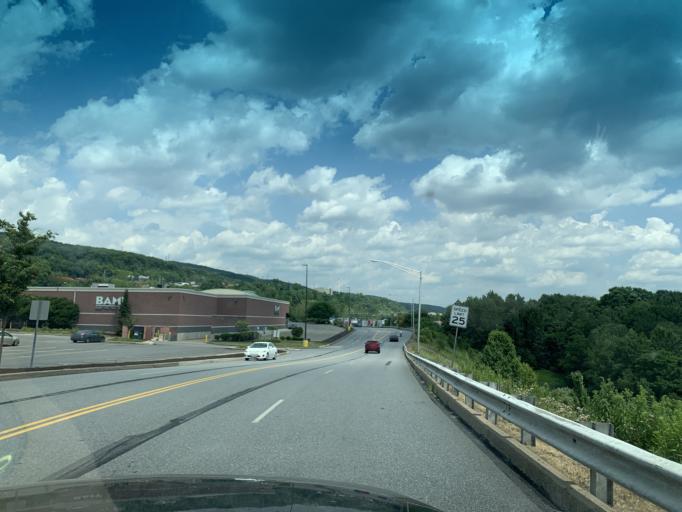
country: US
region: Pennsylvania
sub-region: Lackawanna County
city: Chinchilla
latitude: 41.4593
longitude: -75.6517
